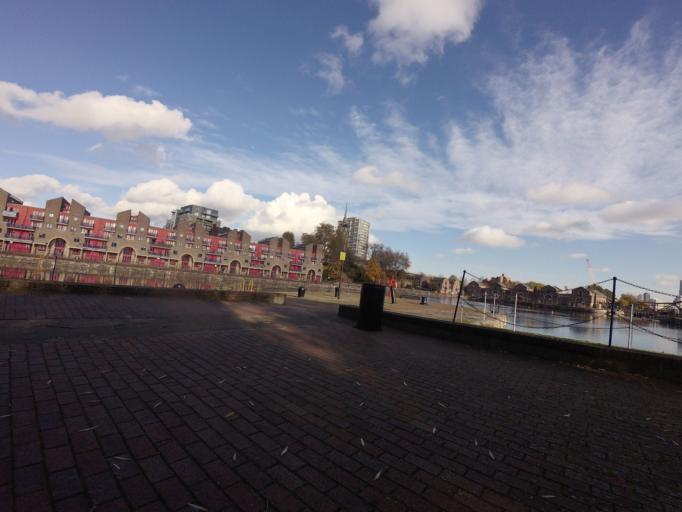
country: GB
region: England
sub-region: Greater London
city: Bethnal Green
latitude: 51.5082
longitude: -0.0541
